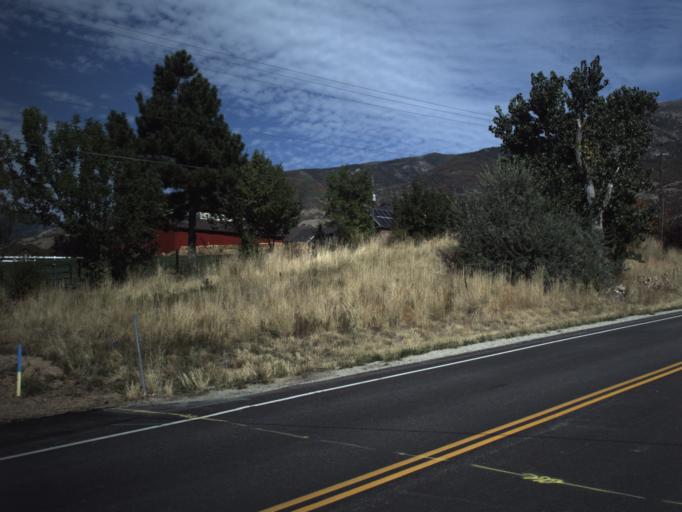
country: US
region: Utah
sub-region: Davis County
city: Kaysville
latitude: 41.0652
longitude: -111.9199
